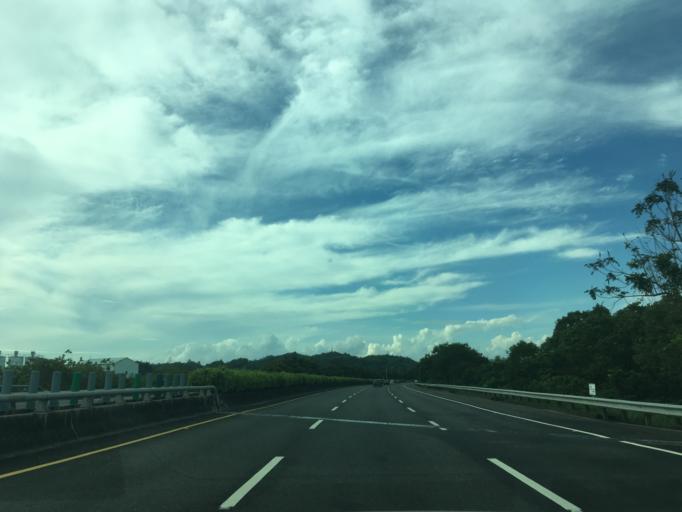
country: TW
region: Taiwan
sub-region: Chiayi
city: Jiayi Shi
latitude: 23.5157
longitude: 120.4852
